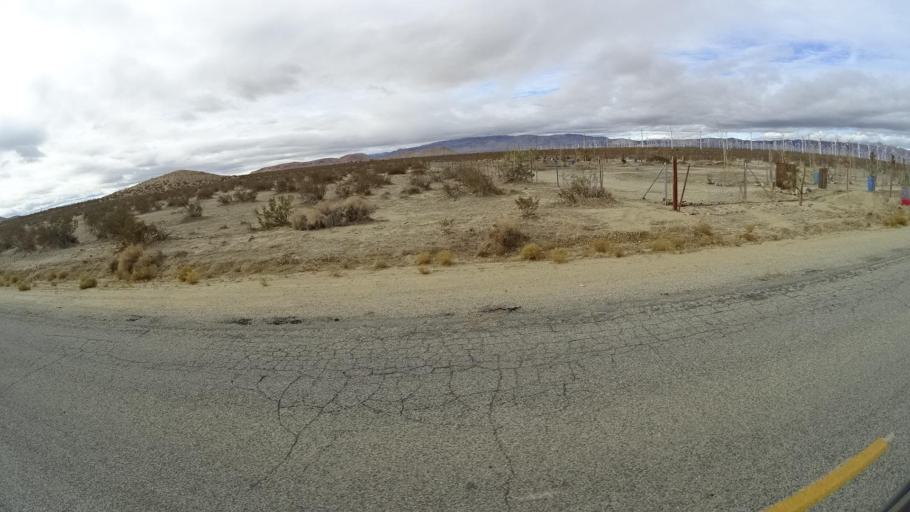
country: US
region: California
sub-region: Kern County
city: Mojave
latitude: 34.9724
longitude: -118.2104
